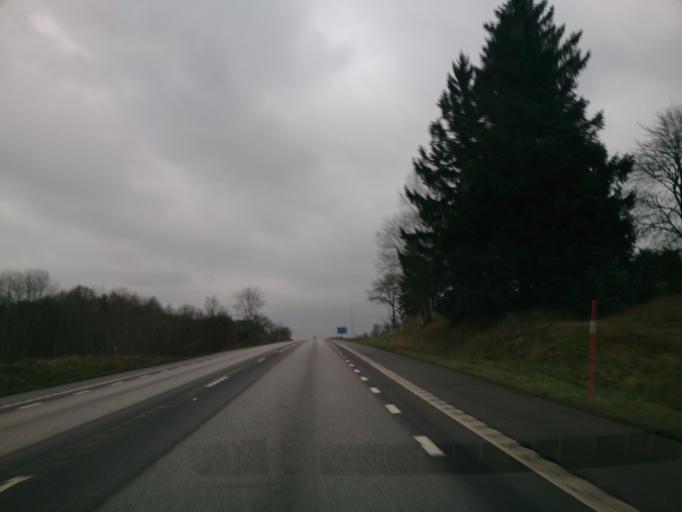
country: SE
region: OEstergoetland
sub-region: Linkopings Kommun
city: Linghem
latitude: 58.4584
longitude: 15.8617
